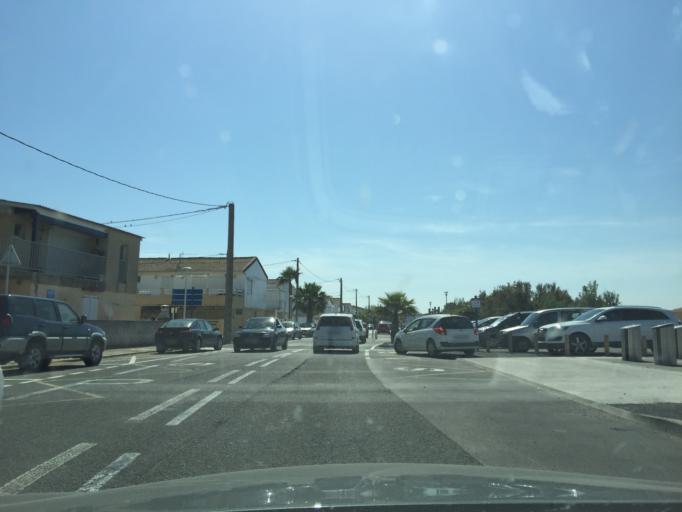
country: FR
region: Languedoc-Roussillon
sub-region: Departement de l'Aude
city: Gruissan
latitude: 43.0983
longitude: 3.1077
